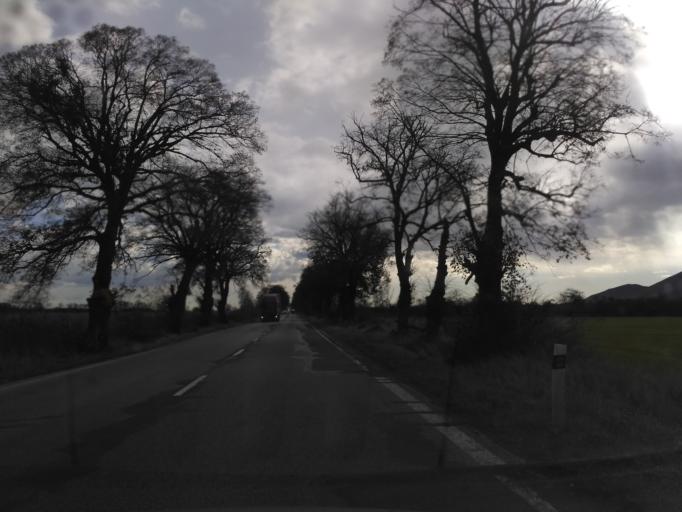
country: HU
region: Borsod-Abauj-Zemplen
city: Satoraljaujhely
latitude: 48.4536
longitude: 21.6477
